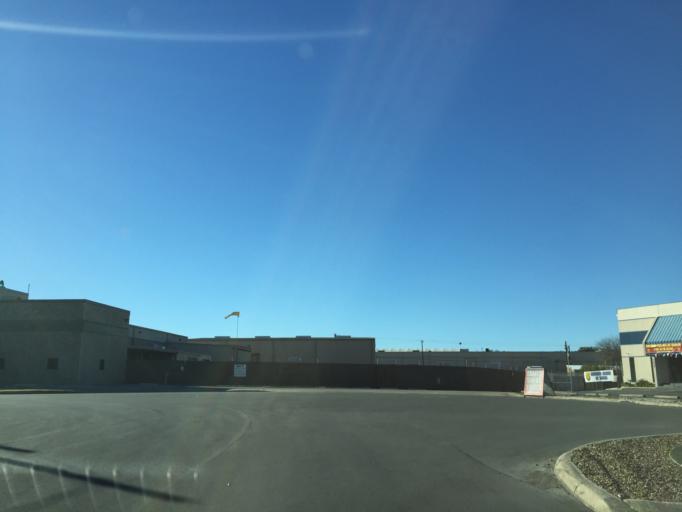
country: US
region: Texas
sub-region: Bexar County
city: Castle Hills
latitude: 29.5527
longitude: -98.4914
